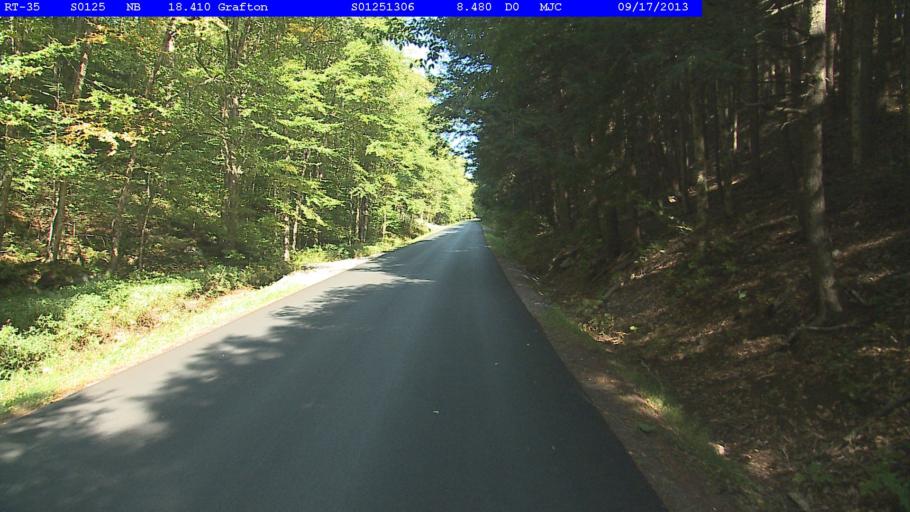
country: US
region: Vermont
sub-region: Windsor County
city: Chester
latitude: 43.2280
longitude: -72.6053
